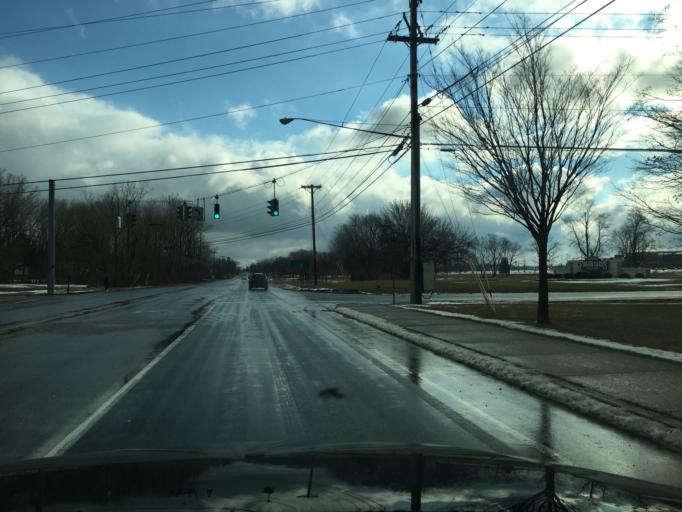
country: US
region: New York
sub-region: Ontario County
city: Victor
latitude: 42.9744
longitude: -77.3494
